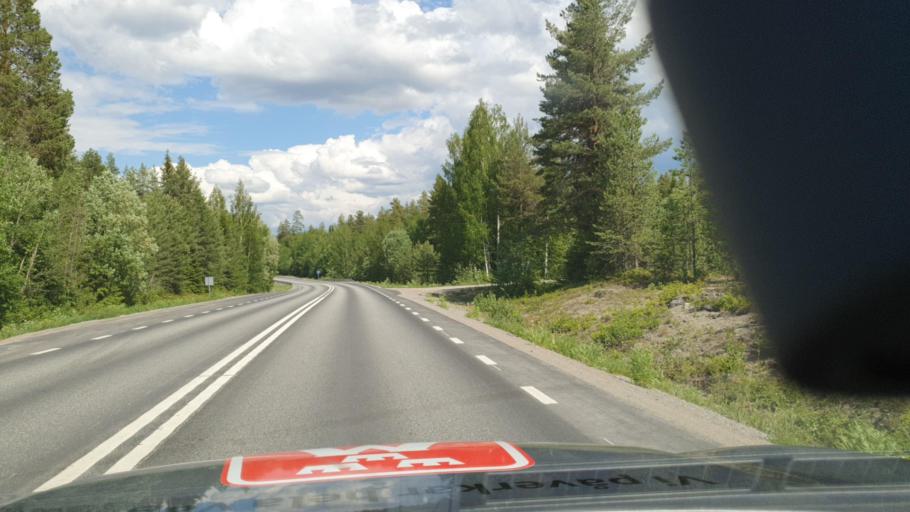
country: SE
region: Vaesternorrland
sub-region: Solleftea Kommun
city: As
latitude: 63.6698
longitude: 16.7921
